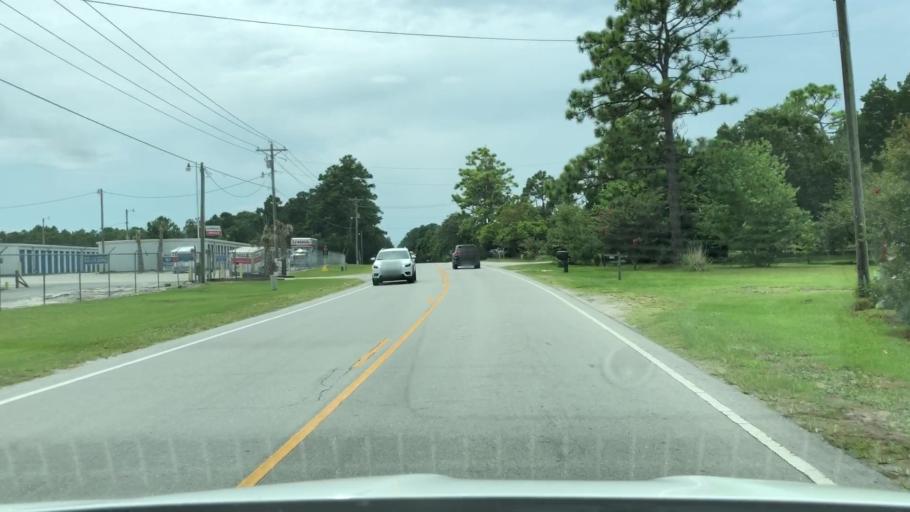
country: US
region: North Carolina
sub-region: Carteret County
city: Broad Creek
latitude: 34.7334
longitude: -76.8891
